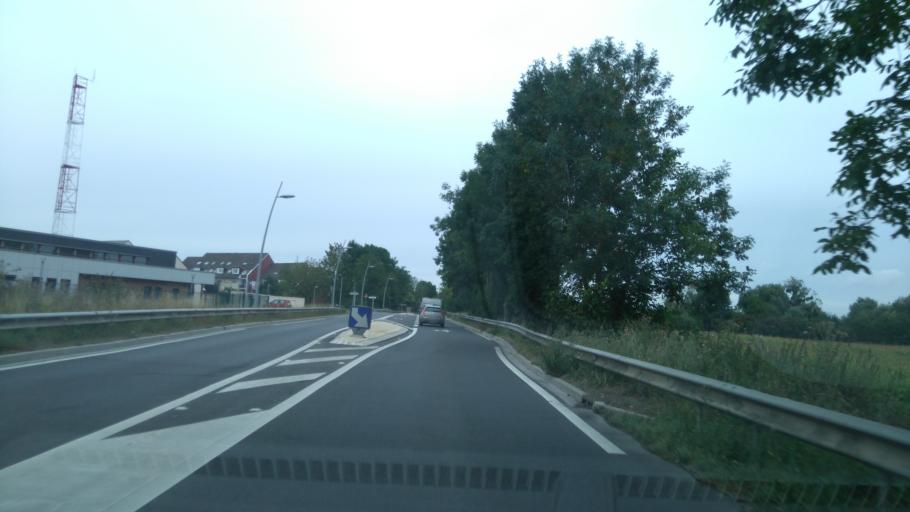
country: FR
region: Picardie
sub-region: Departement de l'Oise
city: Villers-sous-Saint-Leu
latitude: 49.2111
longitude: 2.4070
